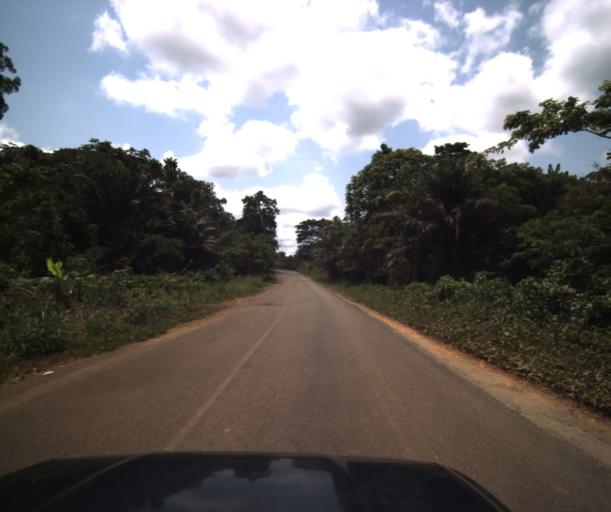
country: CM
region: Centre
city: Eseka
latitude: 3.8235
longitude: 10.8048
